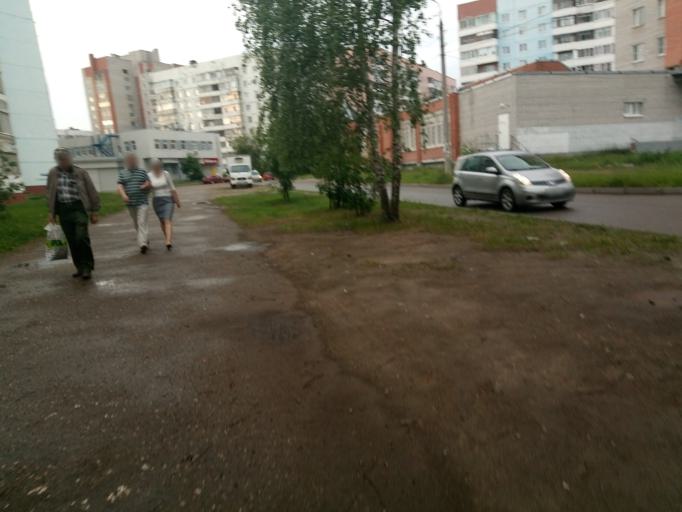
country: RU
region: Jaroslavl
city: Yaroslavl
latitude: 57.6502
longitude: 39.9589
